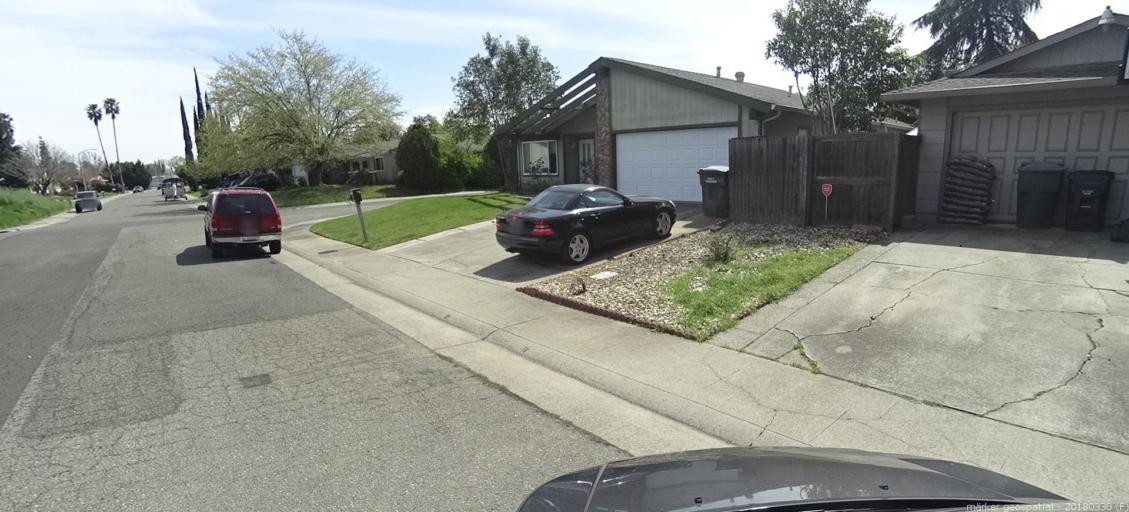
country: US
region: California
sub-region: Sacramento County
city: Rosemont
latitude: 38.5402
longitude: -121.3692
